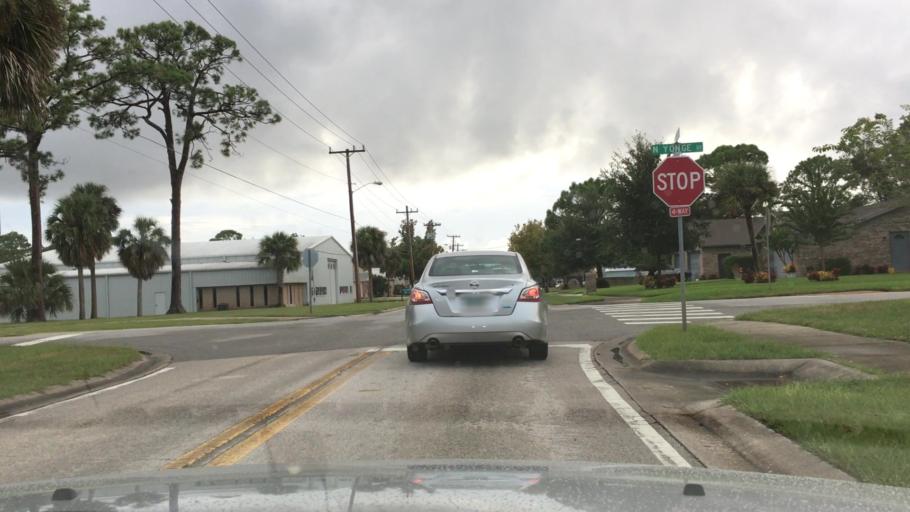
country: US
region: Florida
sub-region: Volusia County
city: Ormond Beach
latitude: 29.2919
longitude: -81.0666
